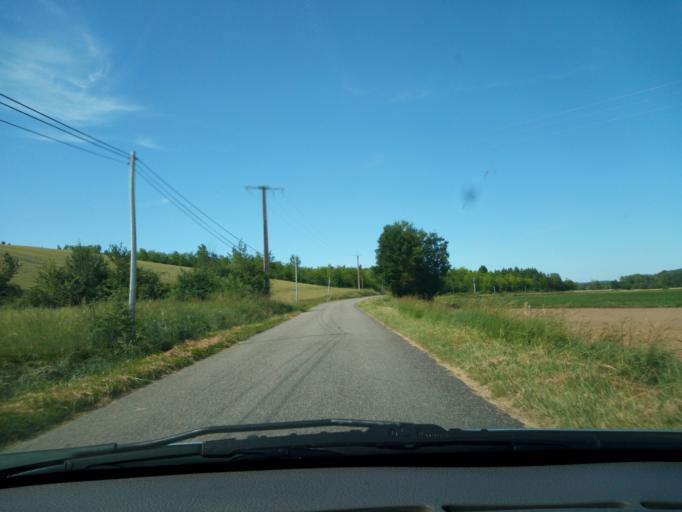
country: FR
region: Midi-Pyrenees
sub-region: Departement du Lot
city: Castelnau-Montratier
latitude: 44.2322
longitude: 1.3301
